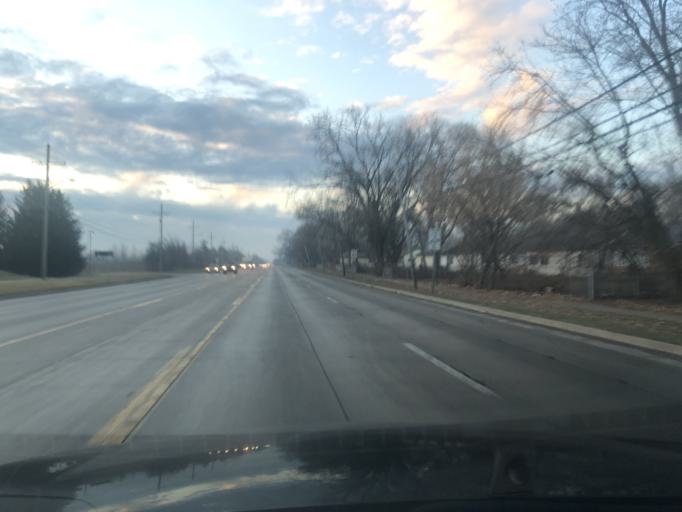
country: US
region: Michigan
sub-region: Wayne County
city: Garden City
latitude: 42.2958
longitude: -83.3493
